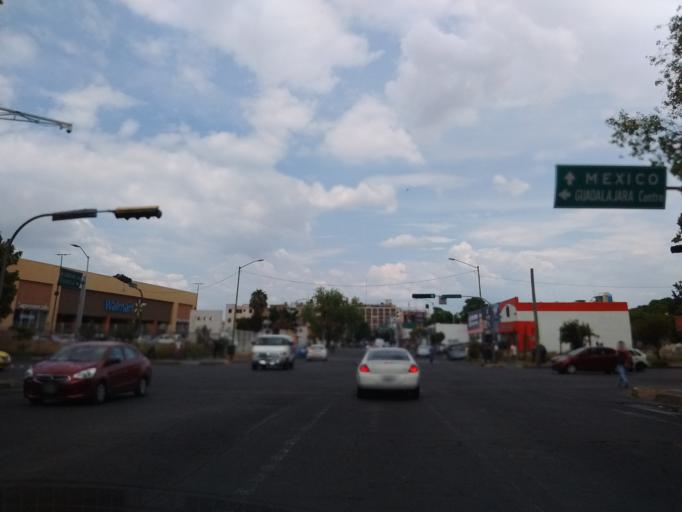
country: MX
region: Jalisco
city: Guadalajara
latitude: 20.6639
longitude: -103.3496
